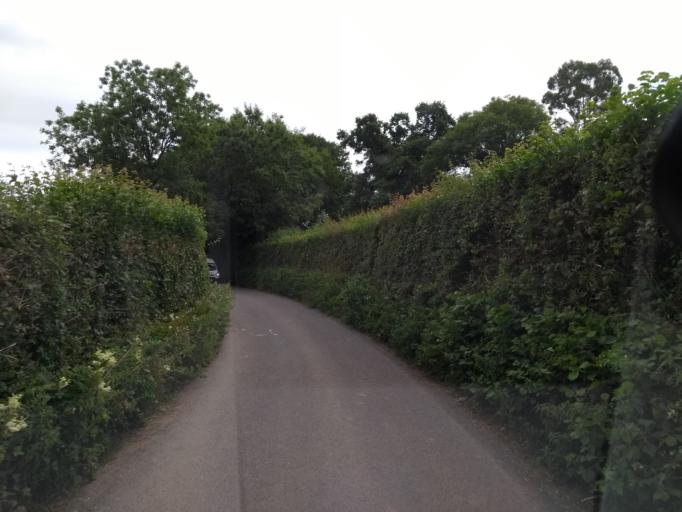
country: GB
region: England
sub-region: Somerset
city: Bishops Lydeard
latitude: 51.0490
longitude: -3.2213
